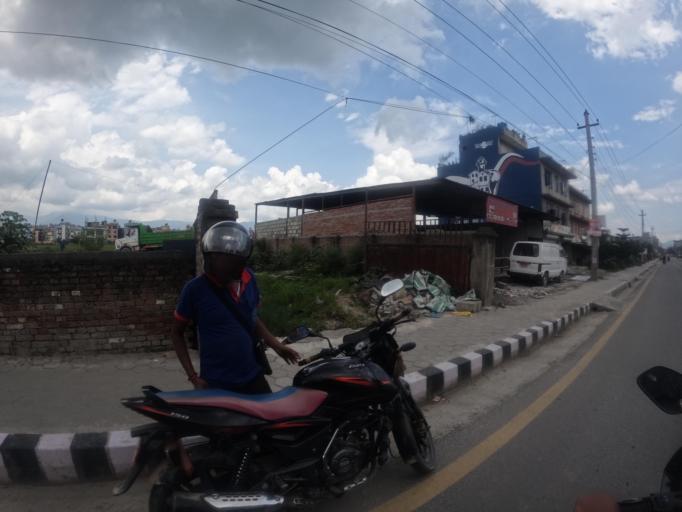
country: NP
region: Central Region
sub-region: Bagmati Zone
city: Bhaktapur
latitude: 27.6799
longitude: 85.3987
